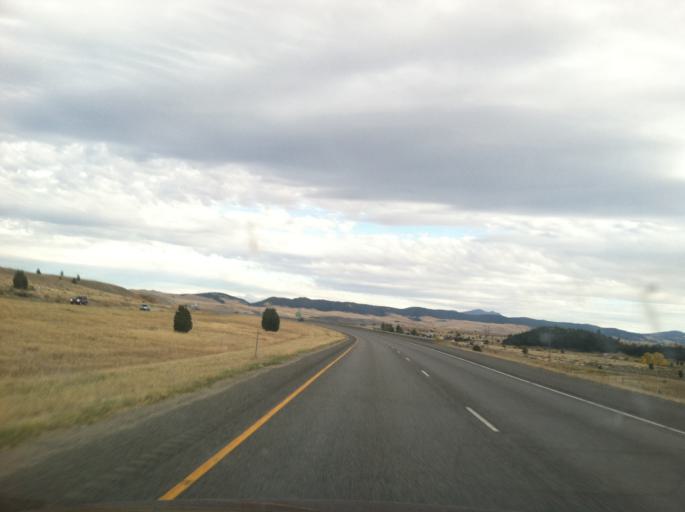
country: US
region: Montana
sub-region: Silver Bow County
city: Butte-Silver Bow (Balance)
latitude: 46.0133
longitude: -112.7138
